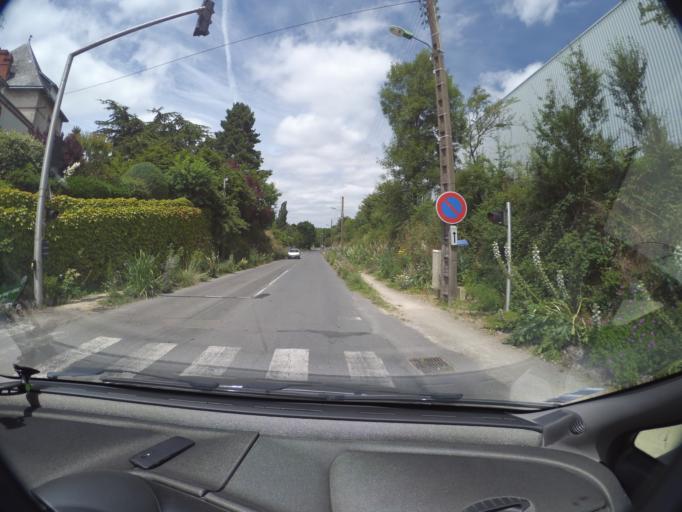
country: FR
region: Pays de la Loire
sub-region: Departement de la Loire-Atlantique
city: Gorges
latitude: 47.1032
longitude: -1.3044
